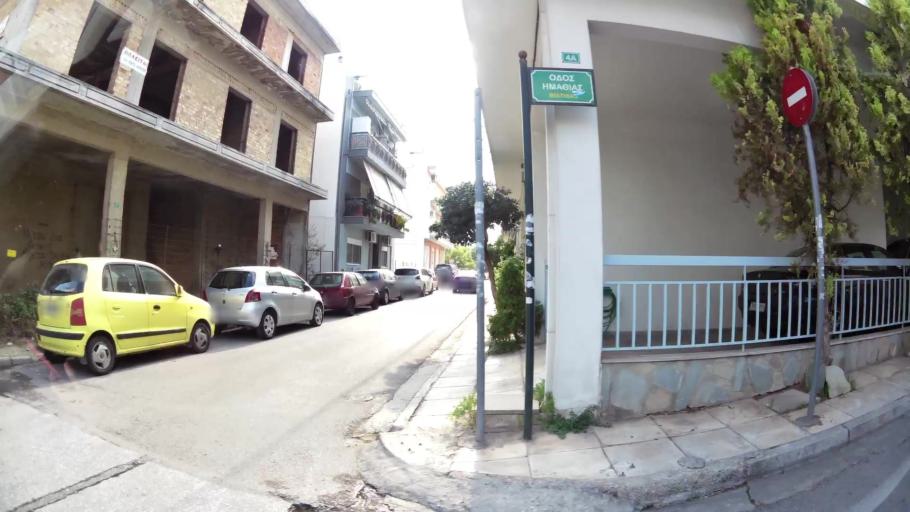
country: GR
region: Attica
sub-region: Nomarchia Athinas
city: Ilion
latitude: 38.0401
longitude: 23.6950
